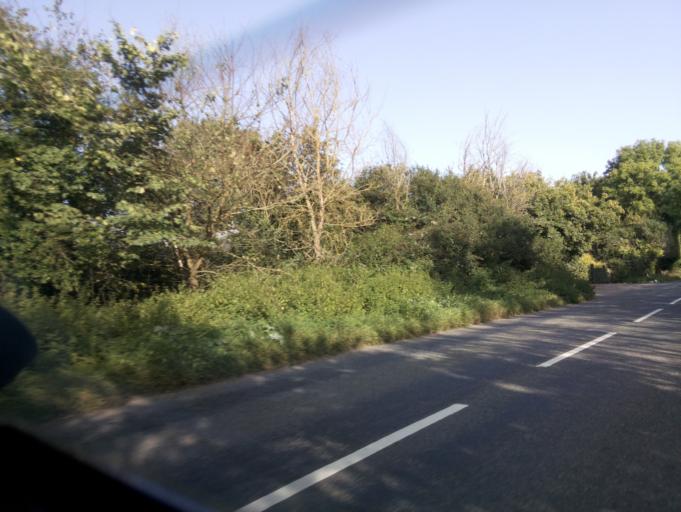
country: GB
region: England
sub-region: Gloucestershire
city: Tewkesbury
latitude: 51.9445
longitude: -2.2083
